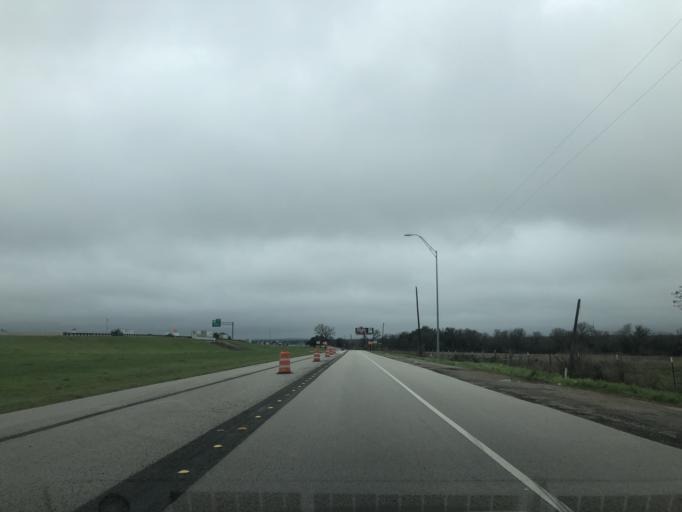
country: US
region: Texas
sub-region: Williamson County
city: Serenada
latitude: 30.7262
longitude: -97.6440
